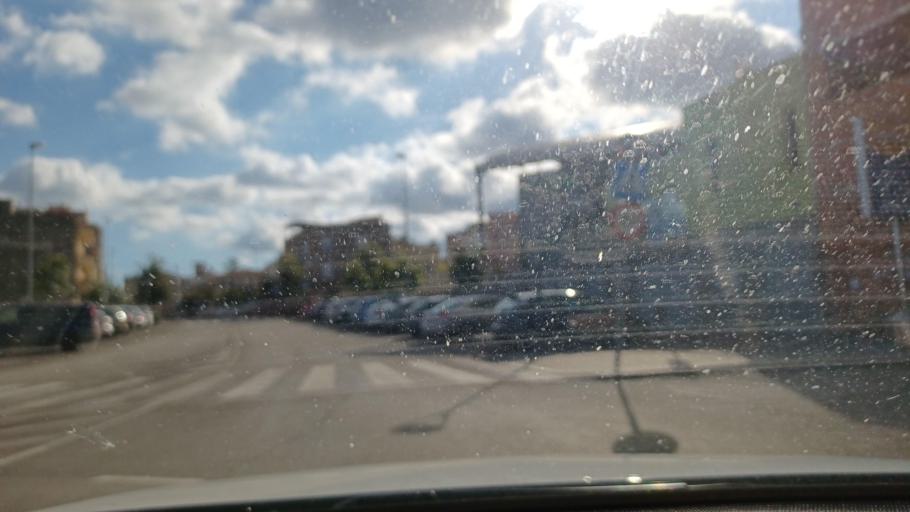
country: ES
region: Valencia
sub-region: Provincia de Castello
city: Betxi
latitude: 39.9310
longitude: -0.1969
